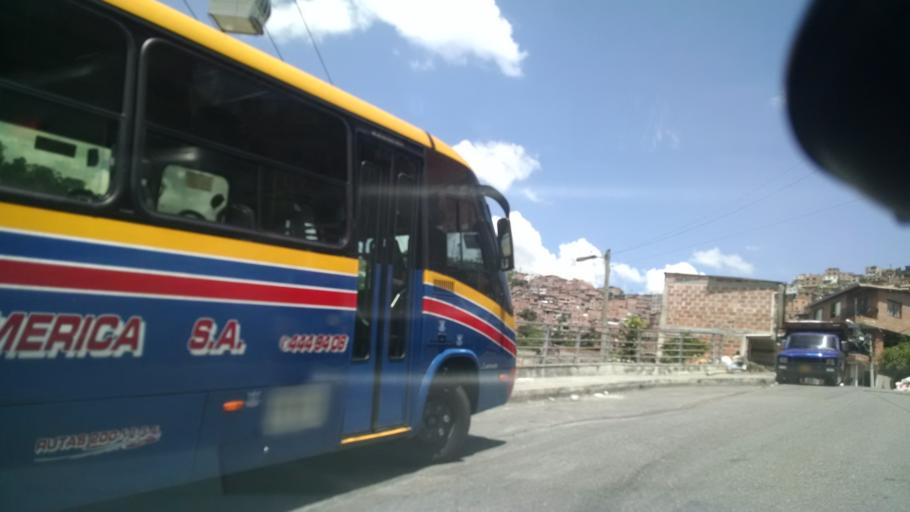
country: CO
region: Antioquia
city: Medellin
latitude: 6.2632
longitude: -75.6135
